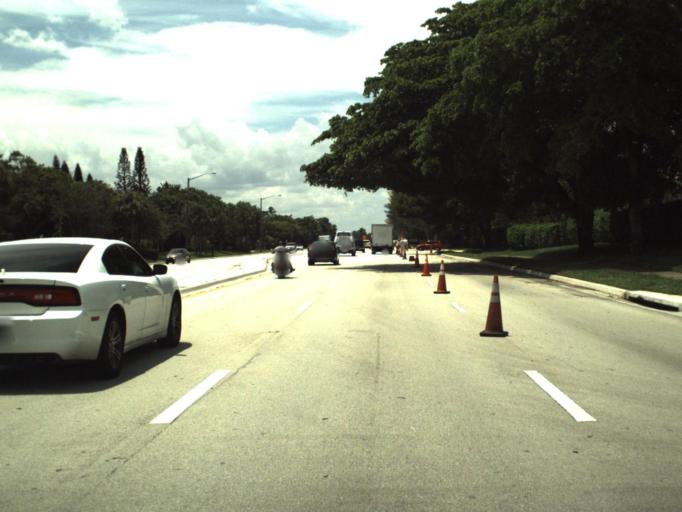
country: US
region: Florida
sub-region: Broward County
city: Tamarac
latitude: 26.2407
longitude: -80.2585
